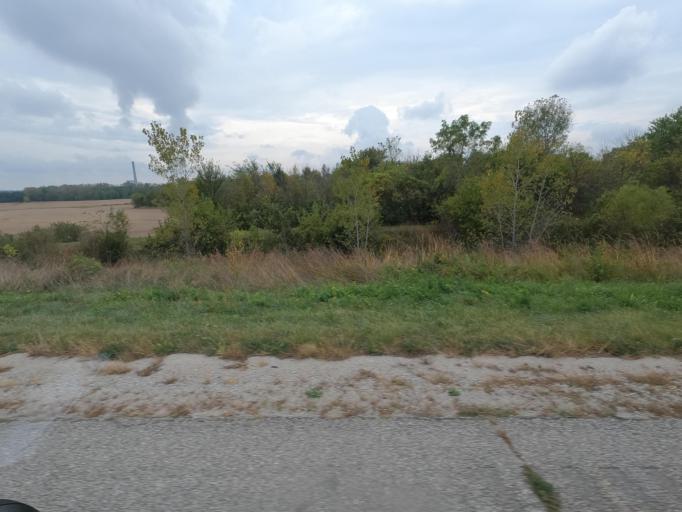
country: US
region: Iowa
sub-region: Wapello County
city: Eddyville
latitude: 41.1182
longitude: -92.5506
